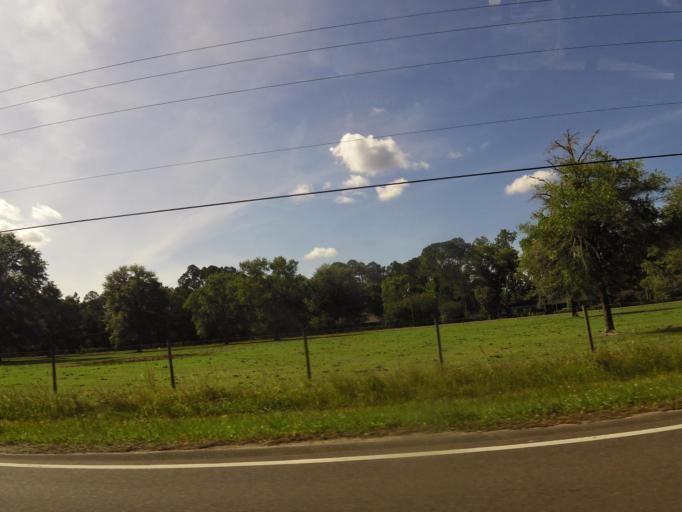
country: US
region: Florida
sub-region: Nassau County
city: Callahan
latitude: 30.5560
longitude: -81.8742
